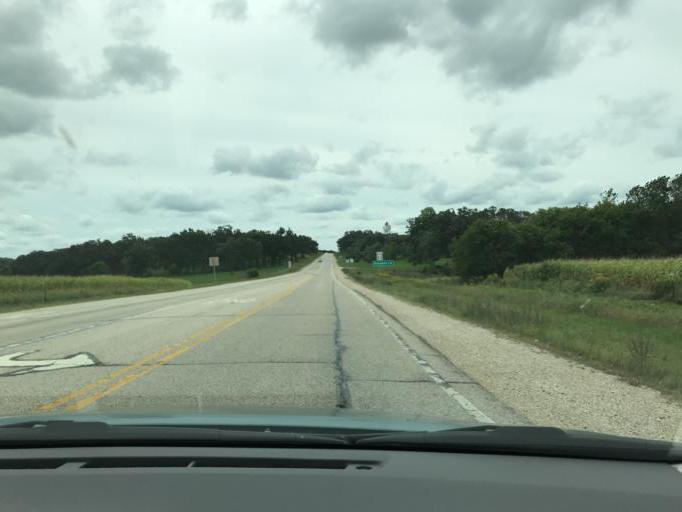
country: US
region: Wisconsin
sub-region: Racine County
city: Bohners Lake
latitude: 42.6112
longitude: -88.2299
